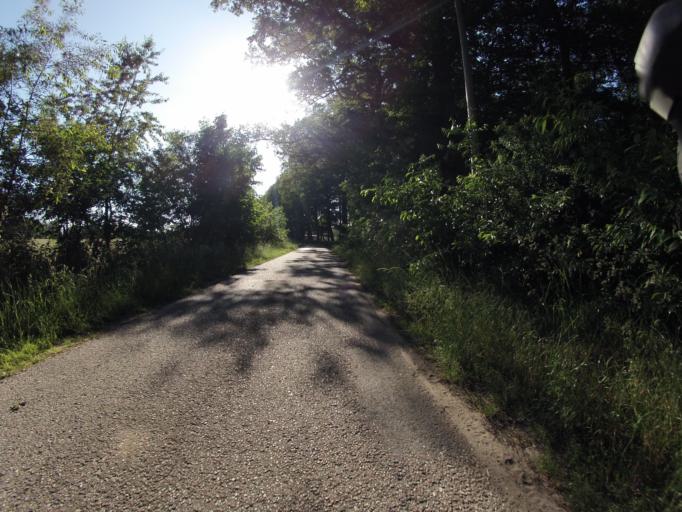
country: DE
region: Lower Saxony
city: Suddendorf
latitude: 52.3146
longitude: 7.2463
